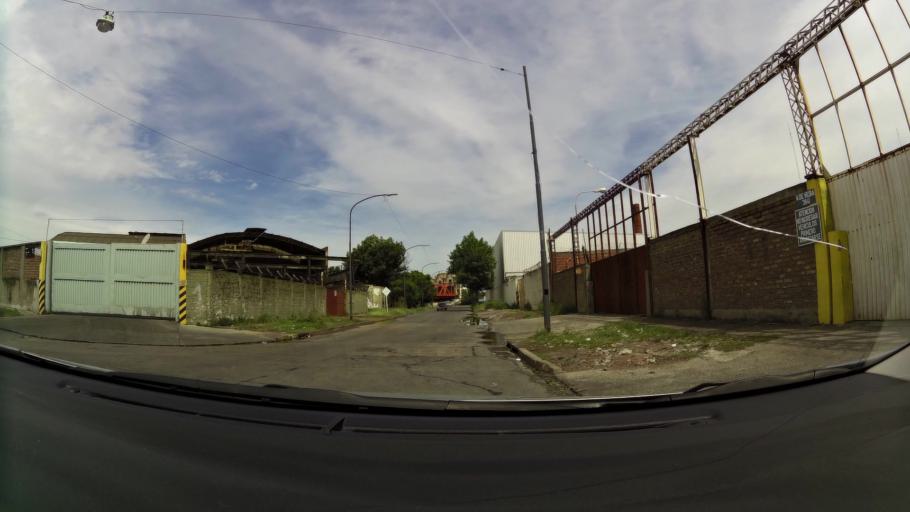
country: AR
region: Buenos Aires
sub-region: Partido de Lanus
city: Lanus
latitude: -34.6584
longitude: -58.4192
